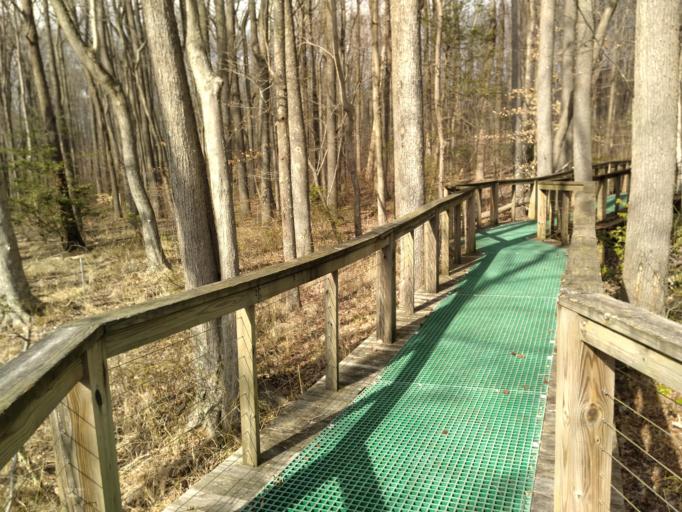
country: US
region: Maryland
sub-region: Anne Arundel County
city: Mayo
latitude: 38.8810
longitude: -76.5514
